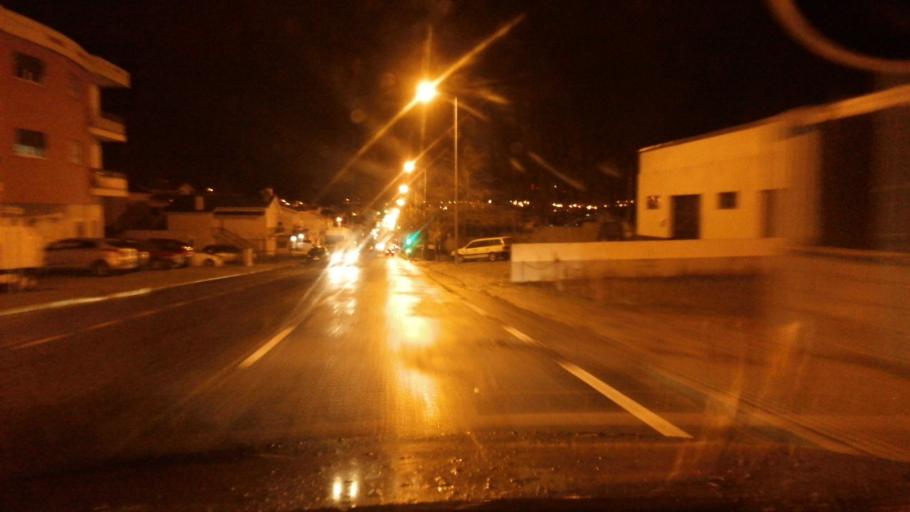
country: PT
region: Viseu
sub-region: Moimenta da Beira
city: Moimenta da Beira
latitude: 40.9735
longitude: -7.6074
